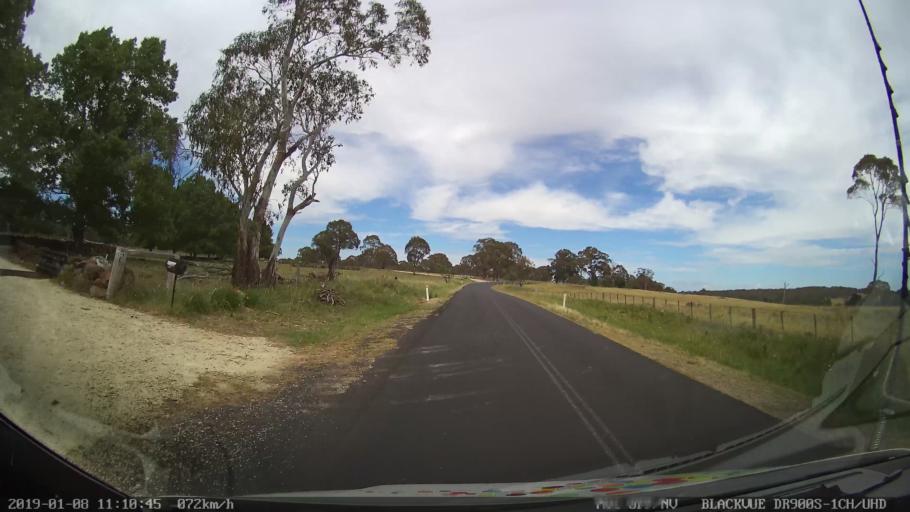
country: AU
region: New South Wales
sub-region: Guyra
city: Guyra
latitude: -30.2261
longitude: 151.6327
